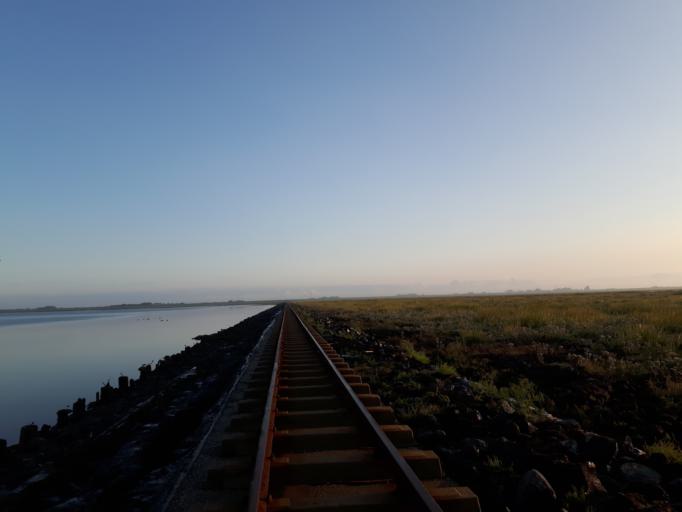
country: DE
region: Schleswig-Holstein
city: Dagebull
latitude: 54.7111
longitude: 8.7113
